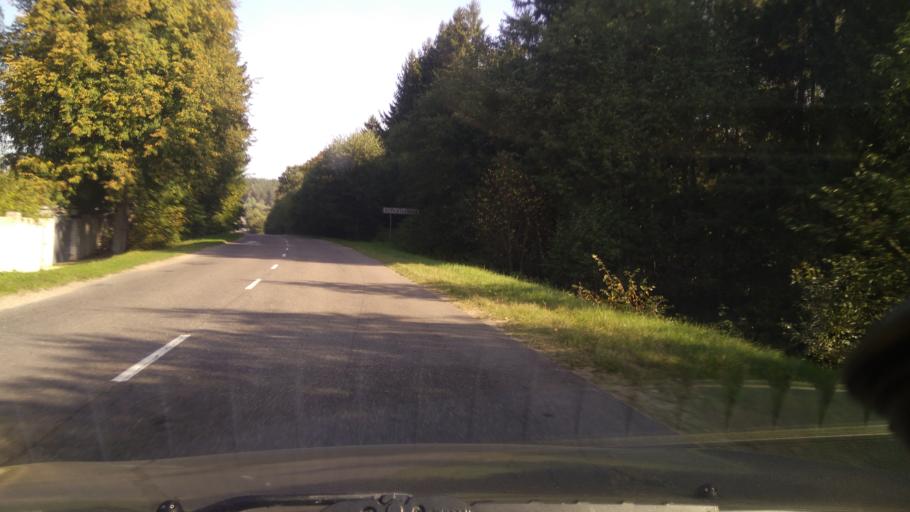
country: BY
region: Minsk
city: Rakaw
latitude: 54.0231
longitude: 27.0536
